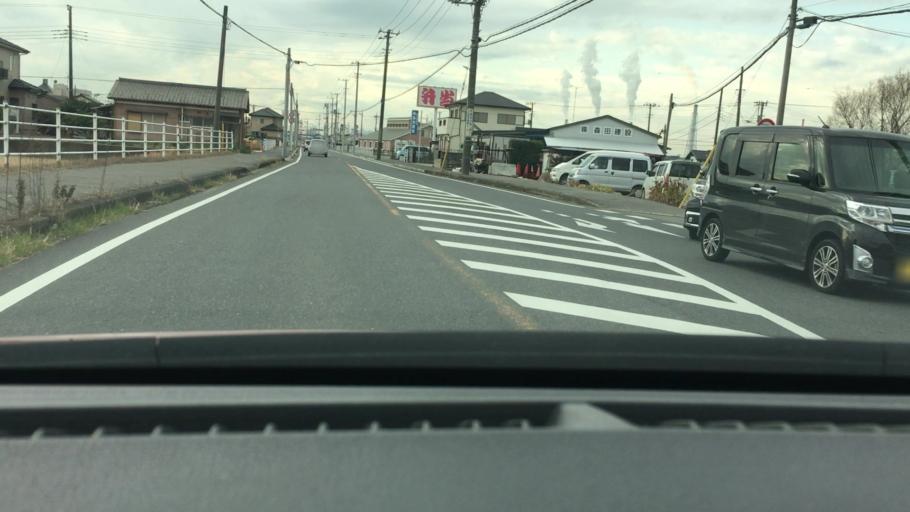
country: JP
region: Chiba
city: Ichihara
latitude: 35.4778
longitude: 140.0602
